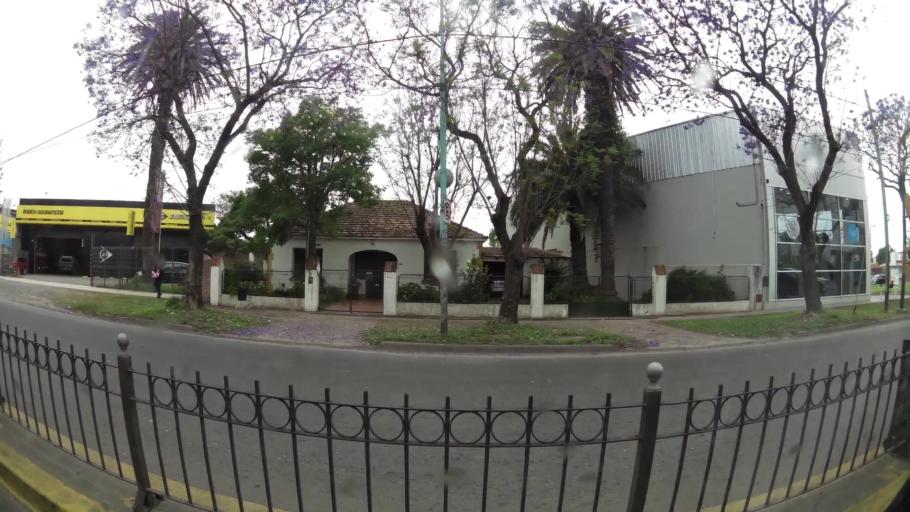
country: AR
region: Buenos Aires
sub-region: Partido de Zarate
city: Zarate
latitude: -34.1152
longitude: -59.0203
